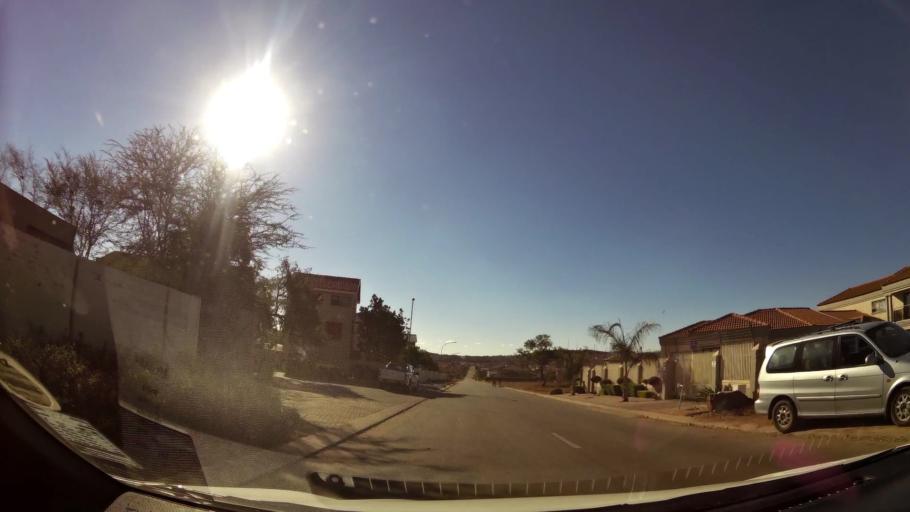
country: ZA
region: Limpopo
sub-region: Capricorn District Municipality
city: Polokwane
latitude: -23.9087
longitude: 29.5031
